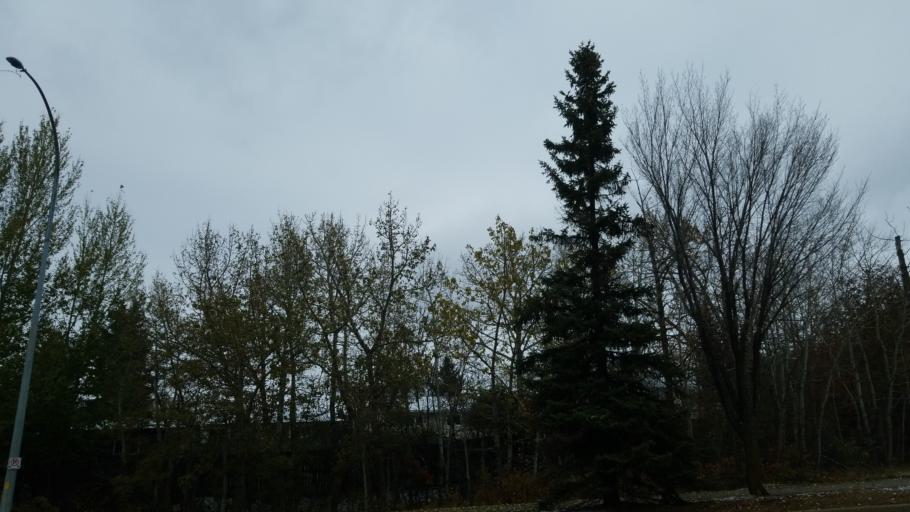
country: CA
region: Alberta
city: Sherwood Park
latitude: 53.5274
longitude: -113.2783
